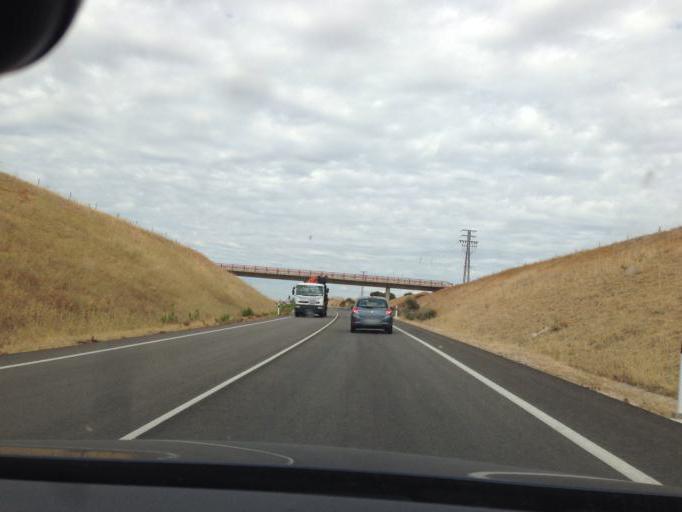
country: ES
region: Madrid
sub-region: Provincia de Madrid
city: Ajalvir
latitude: 40.5534
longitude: -3.4800
